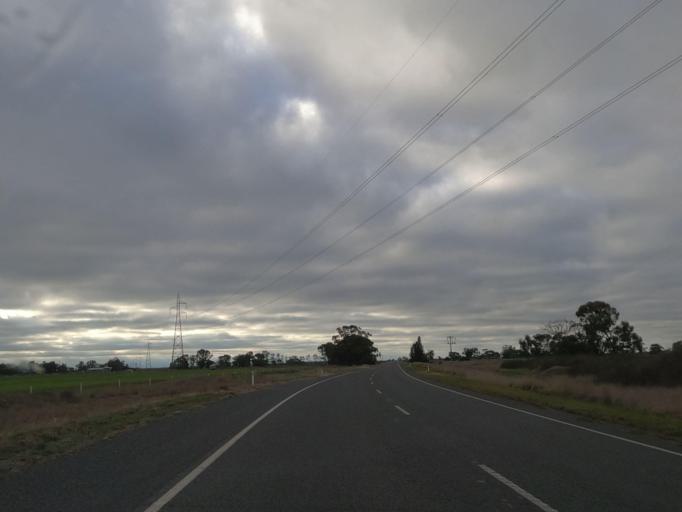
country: AU
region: Victoria
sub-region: Swan Hill
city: Swan Hill
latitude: -35.8634
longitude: 143.9347
